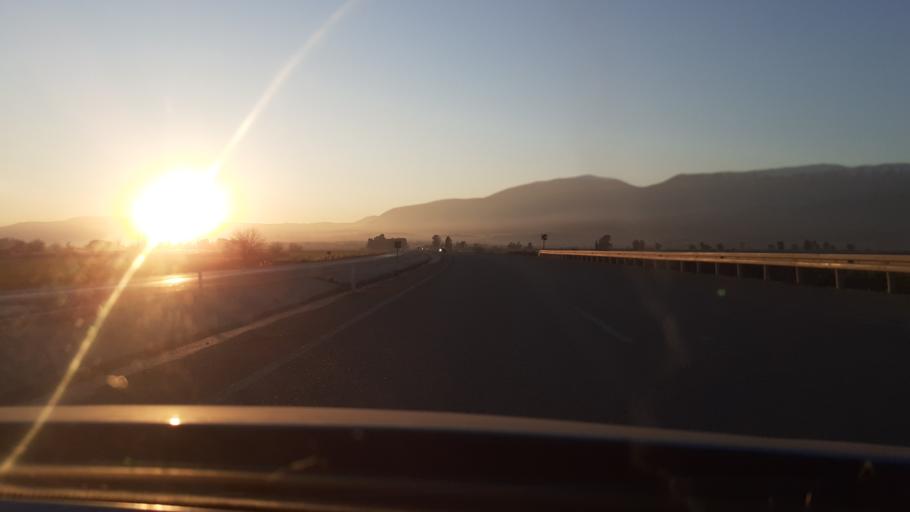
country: TR
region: Hatay
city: Kirikhan
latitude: 36.5069
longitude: 36.4303
